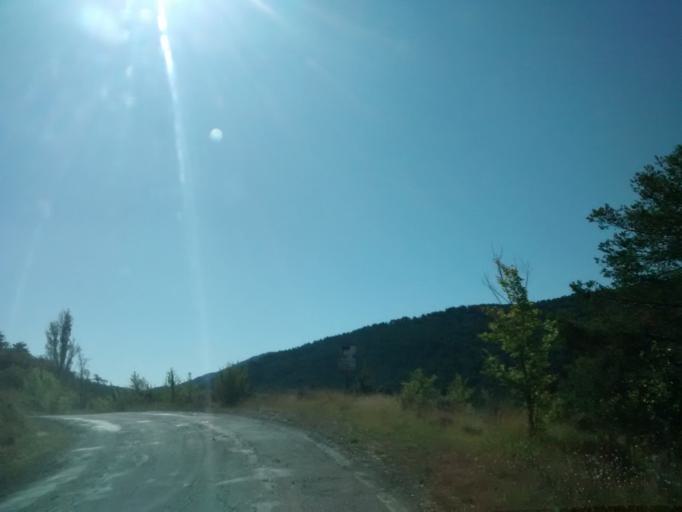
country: ES
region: Aragon
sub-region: Provincia de Huesca
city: Jaca
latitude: 42.5101
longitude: -0.5587
